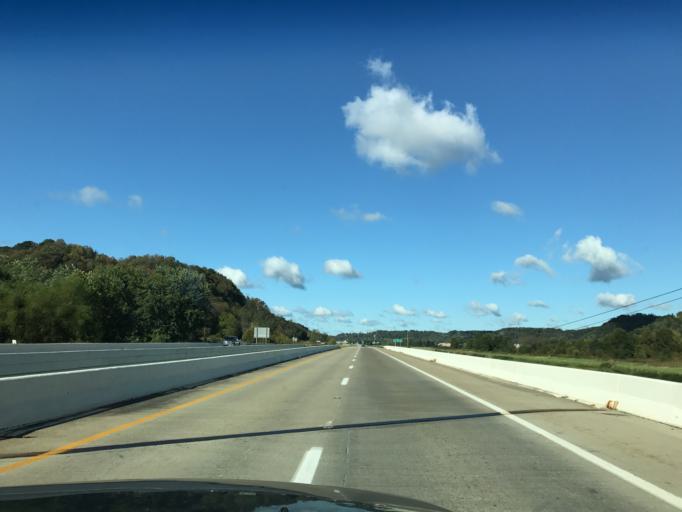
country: US
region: Ohio
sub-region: Athens County
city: Athens
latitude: 39.3315
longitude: -82.0486
